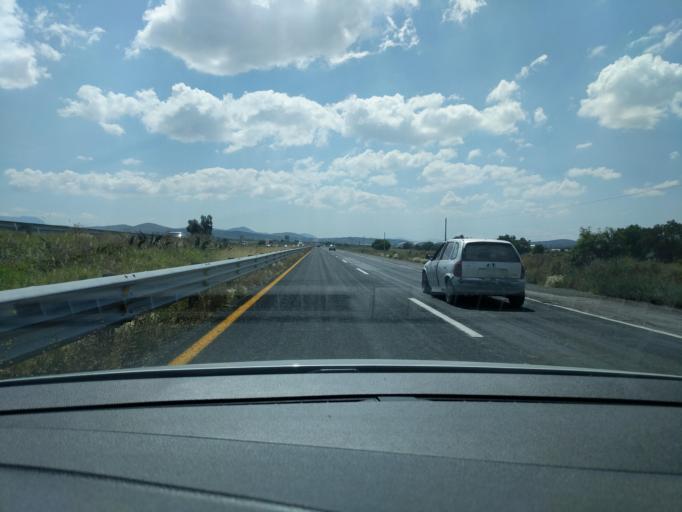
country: MX
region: Hidalgo
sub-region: Mineral de la Reforma
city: Rinconada de los Angeles
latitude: 19.9675
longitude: -98.6975
